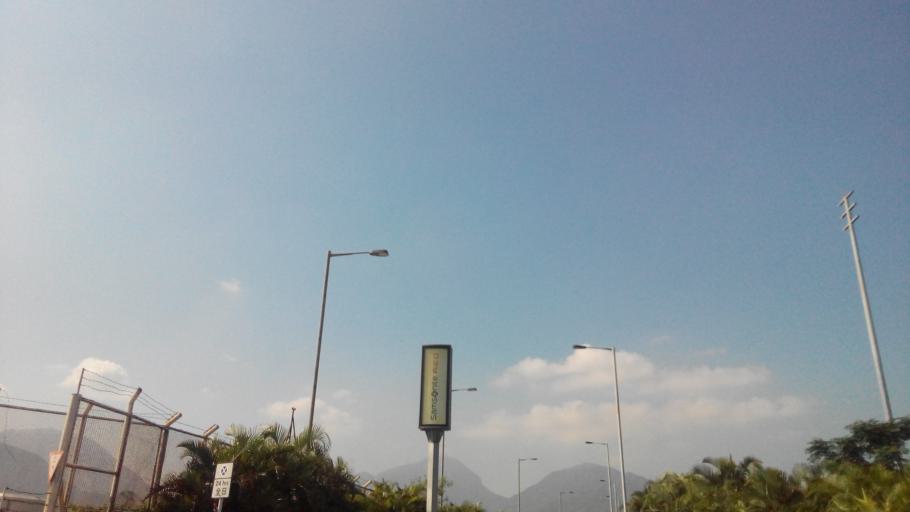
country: HK
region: Tuen Mun
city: Tuen Mun
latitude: 22.3163
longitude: 113.9432
